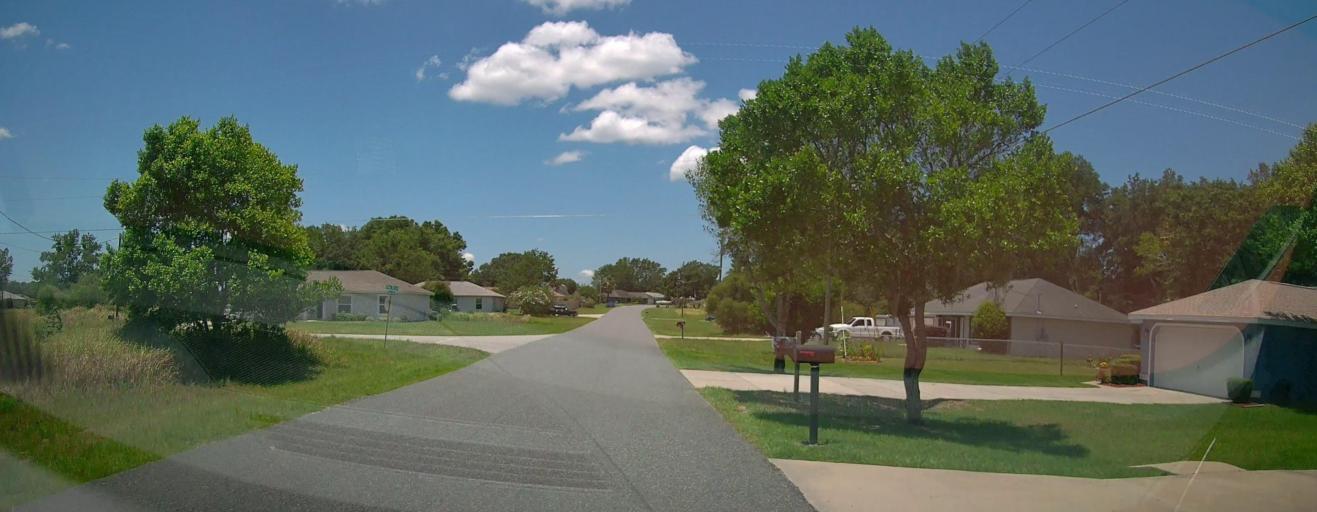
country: US
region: Florida
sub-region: Marion County
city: Silver Springs Shores
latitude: 29.1274
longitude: -82.0429
